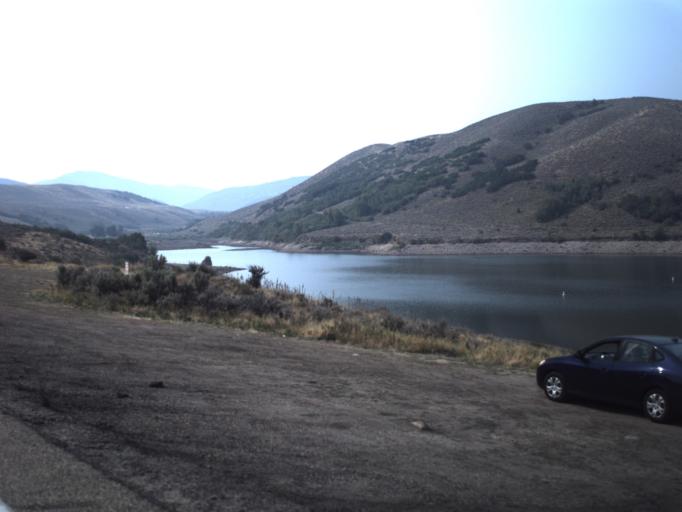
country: US
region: Utah
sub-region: Summit County
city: Summit Park
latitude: 40.8905
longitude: -111.5817
